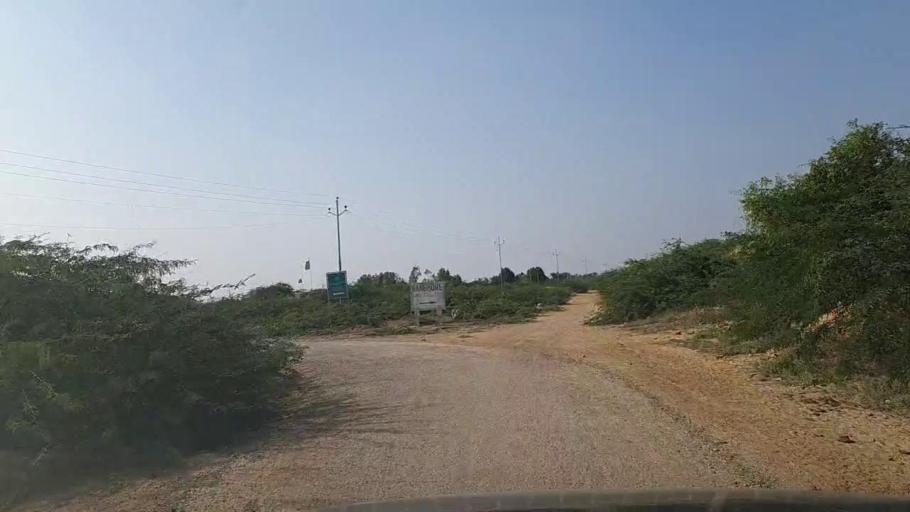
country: PK
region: Sindh
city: Gharo
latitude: 24.7591
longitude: 67.5249
